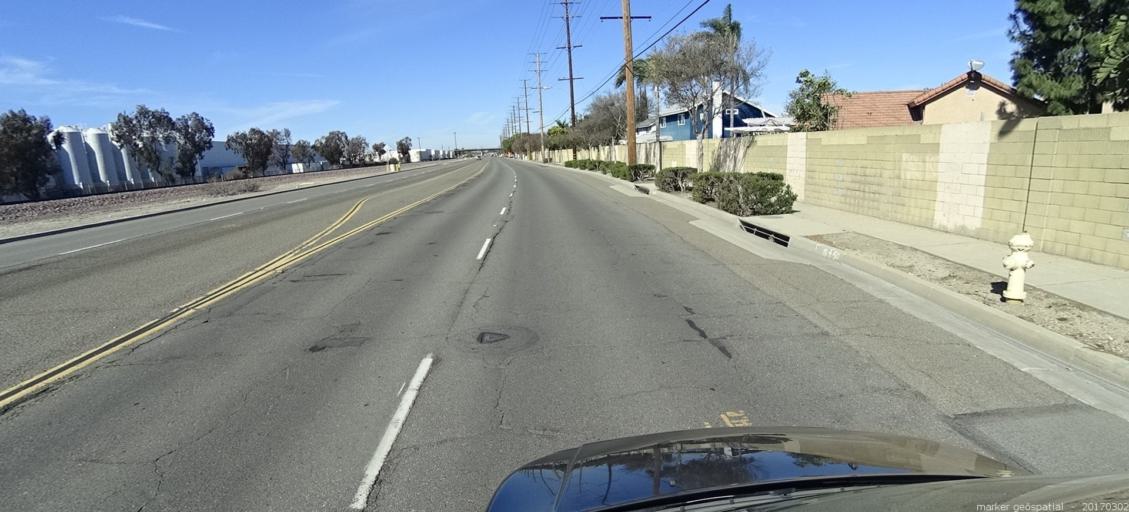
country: US
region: California
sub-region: Orange County
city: Yorba Linda
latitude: 33.8659
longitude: -117.8105
